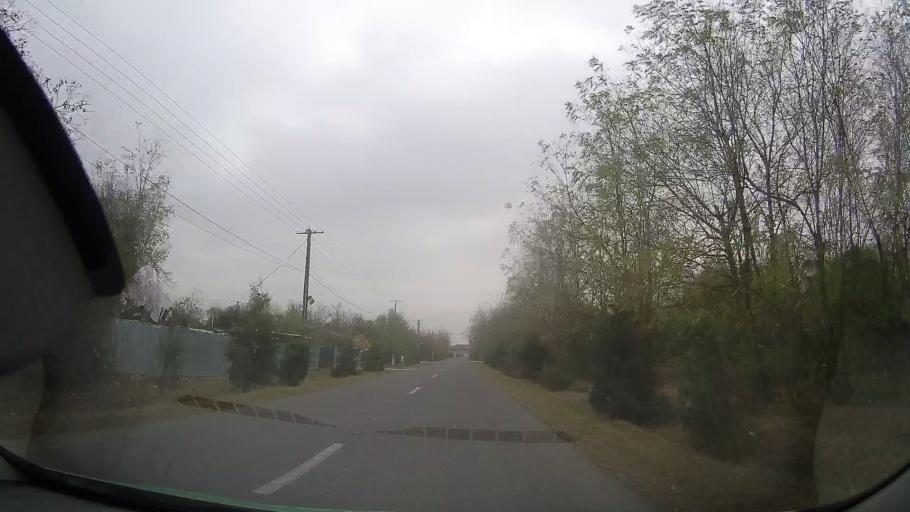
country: RO
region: Buzau
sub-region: Comuna Scutelnici
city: Scutelnici
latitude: 44.8820
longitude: 26.8763
